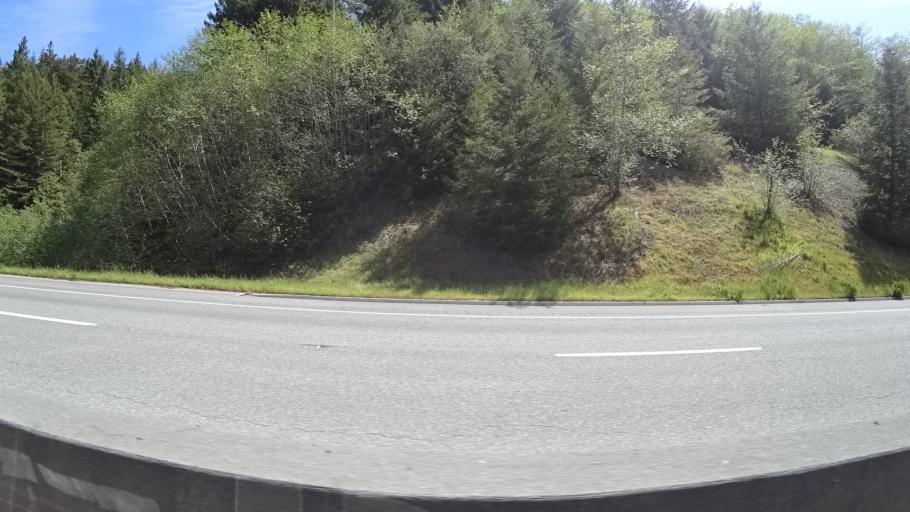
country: US
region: California
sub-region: Humboldt County
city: Westhaven-Moonstone
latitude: 41.3765
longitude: -123.9945
